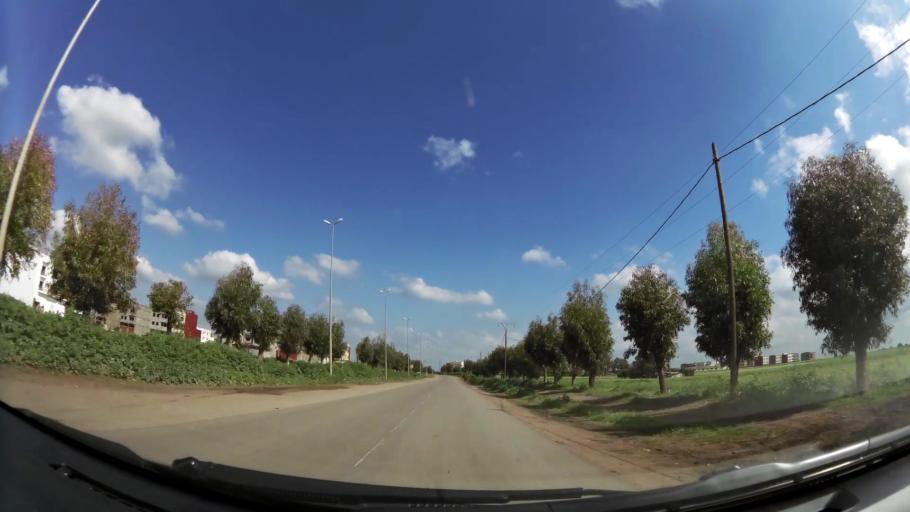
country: MA
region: Grand Casablanca
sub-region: Mediouna
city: Mediouna
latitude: 33.4483
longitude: -7.5054
